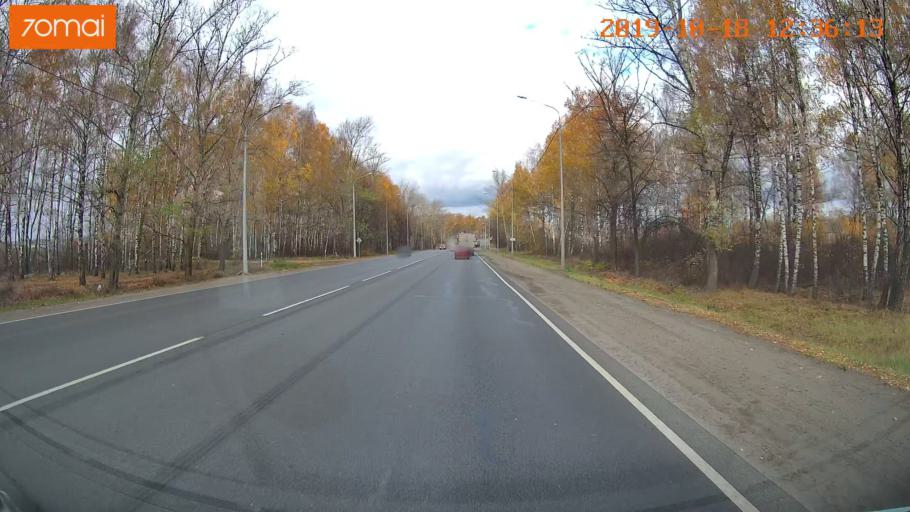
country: RU
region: Rjazan
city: Ryazan'
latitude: 54.6328
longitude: 39.6343
